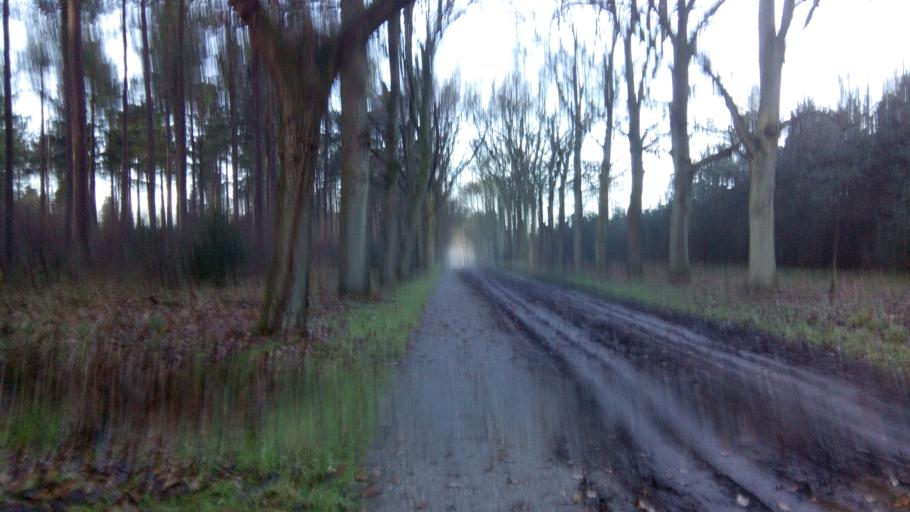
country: NL
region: Utrecht
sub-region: Gemeente Utrechtse Heuvelrug
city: Maarn
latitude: 52.1093
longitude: 5.3758
